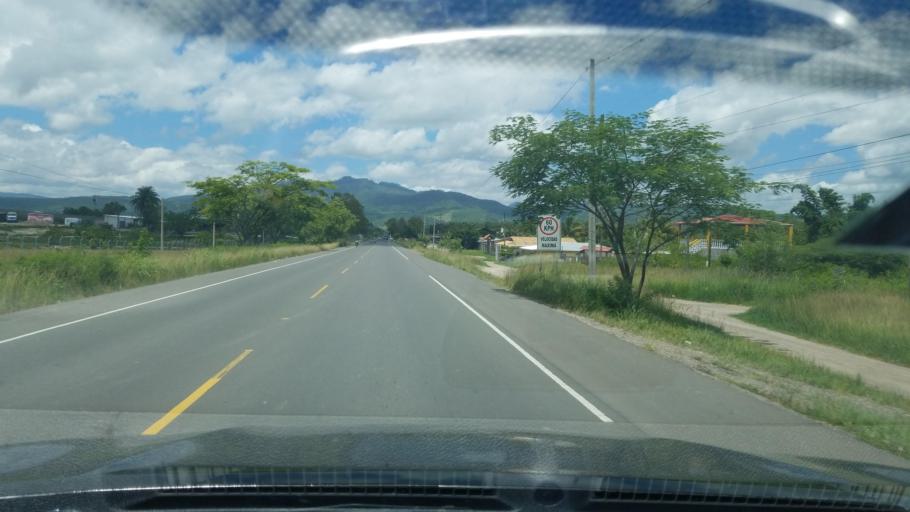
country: HN
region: Francisco Morazan
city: Cofradia
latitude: 14.2901
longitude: -87.2428
